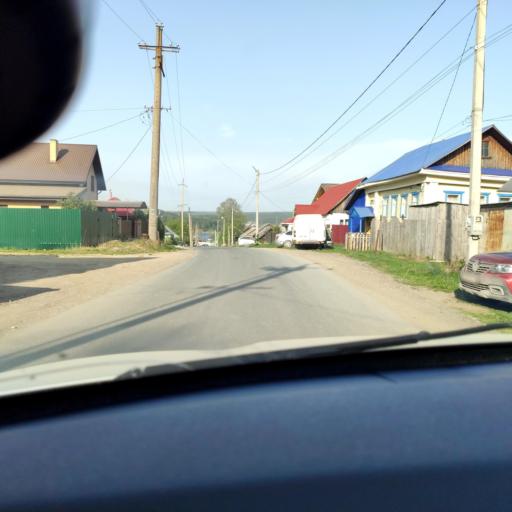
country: RU
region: Perm
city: Polazna
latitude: 58.2993
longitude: 56.4112
